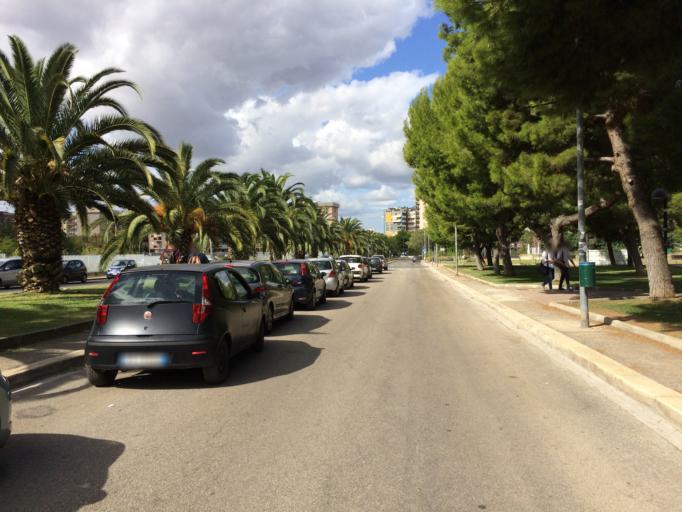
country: IT
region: Apulia
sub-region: Provincia di Bari
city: Bari
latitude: 41.0961
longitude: 16.8587
